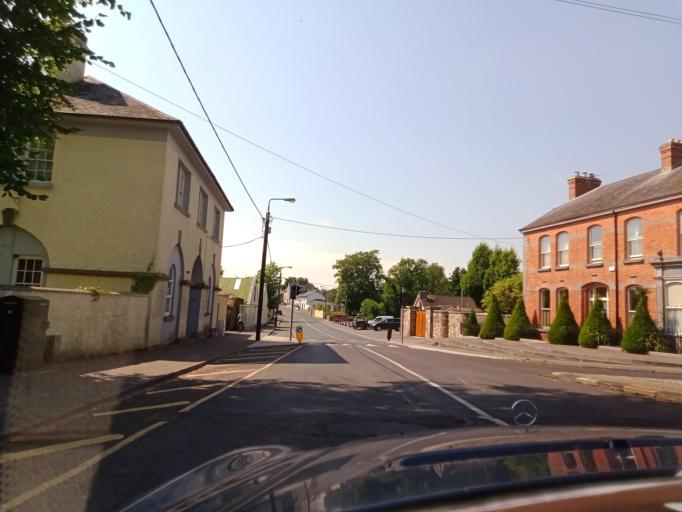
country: IE
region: Leinster
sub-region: Kilkenny
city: Piltown
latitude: 52.3498
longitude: -7.3250
